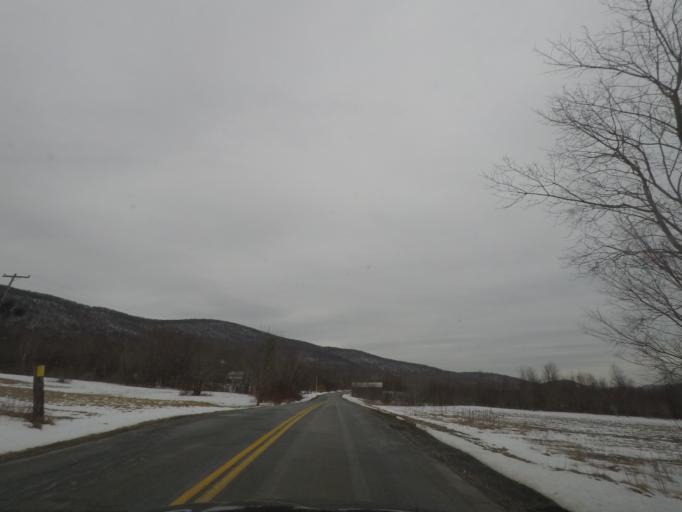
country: US
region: Massachusetts
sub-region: Berkshire County
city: Lanesborough
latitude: 42.5869
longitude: -73.3545
